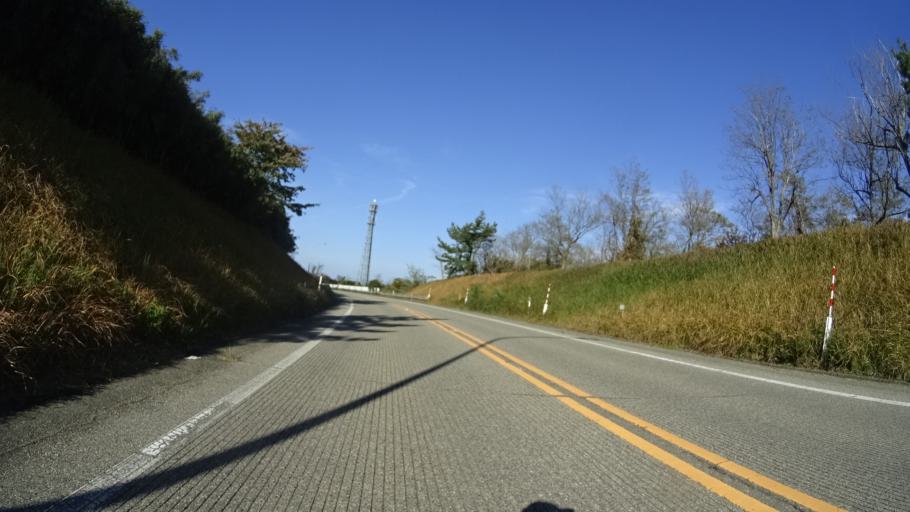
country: JP
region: Ishikawa
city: Kanazawa-shi
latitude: 36.6459
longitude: 136.6365
